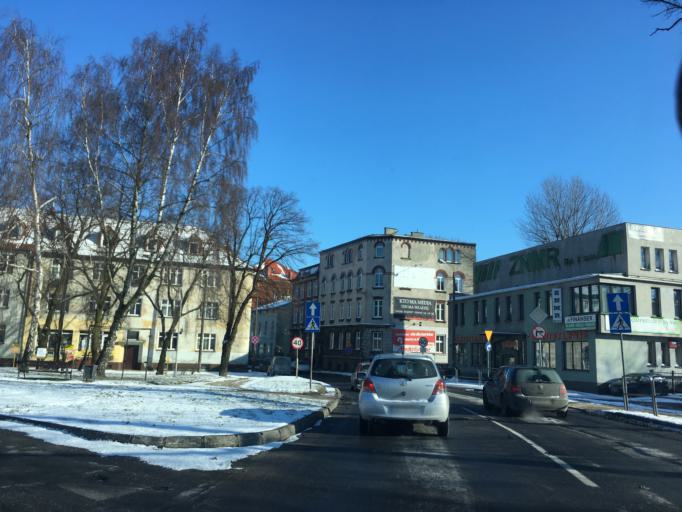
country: PL
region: Pomeranian Voivodeship
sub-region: Slupsk
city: Slupsk
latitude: 54.4640
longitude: 17.0212
